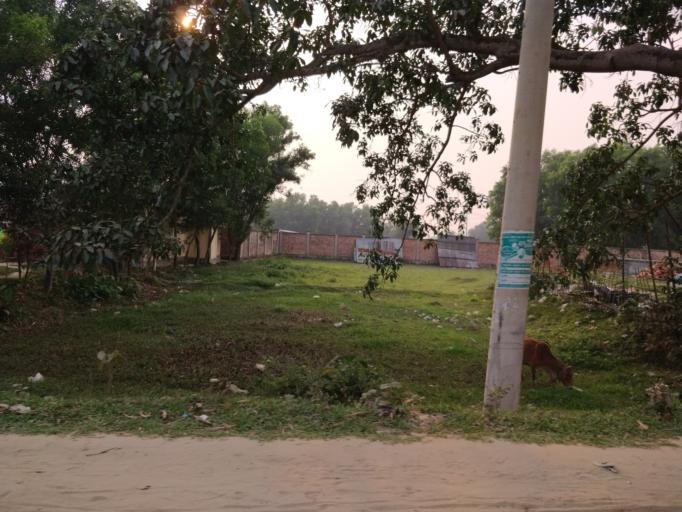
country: BD
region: Sylhet
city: Habiganj
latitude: 24.1478
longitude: 91.3514
